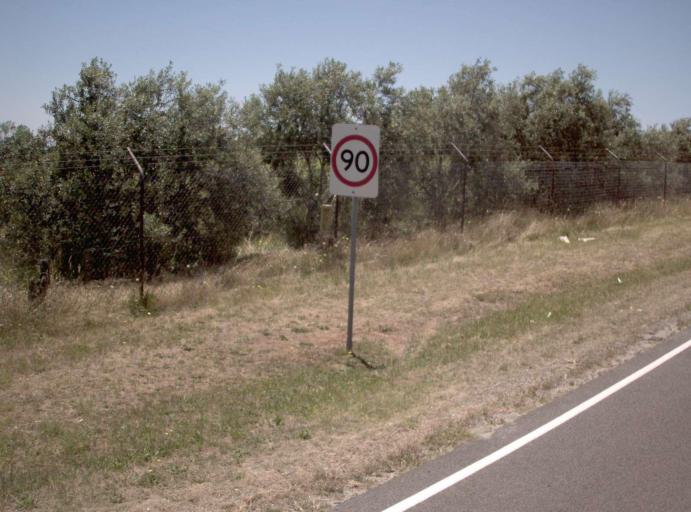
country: AU
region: Victoria
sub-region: Mornington Peninsula
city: Mornington
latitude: -38.2108
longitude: 145.0688
